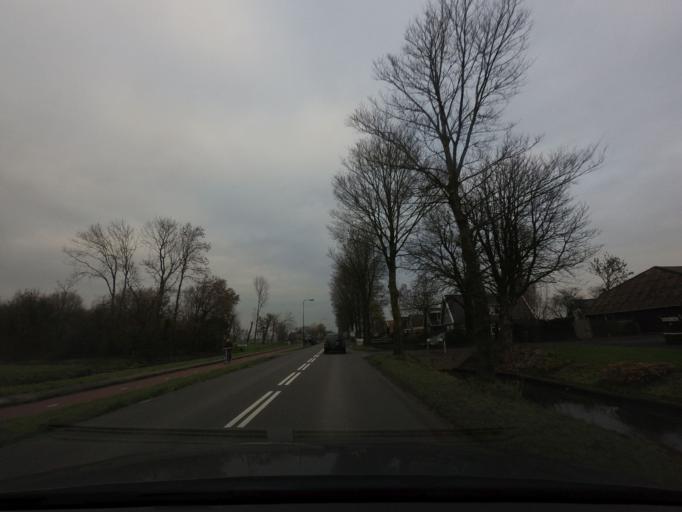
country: NL
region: North Holland
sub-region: Gemeente Heerhugowaard
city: Heerhugowaard
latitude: 52.6851
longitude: 4.8499
